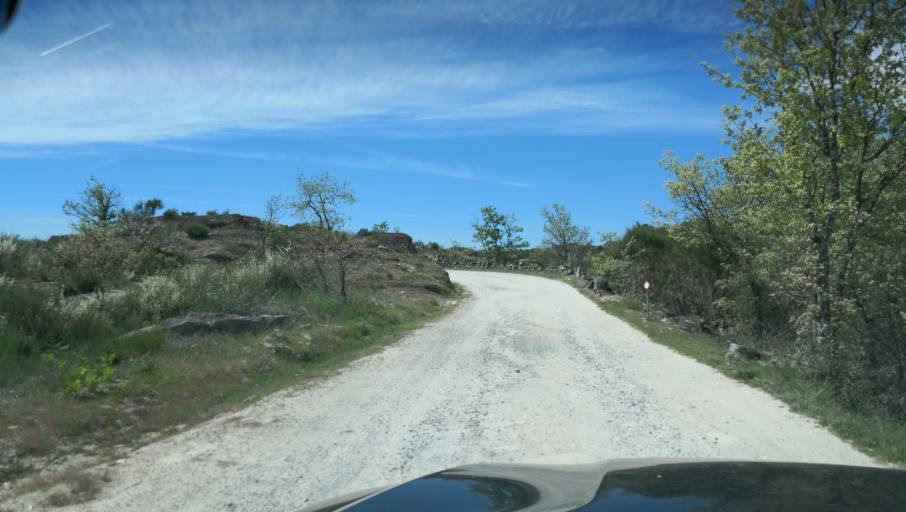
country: PT
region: Vila Real
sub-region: Vila Real
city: Vila Real
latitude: 41.3706
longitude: -7.6720
